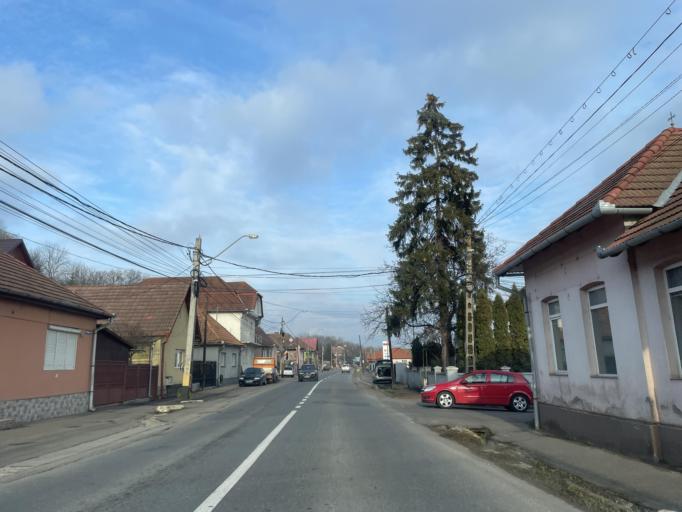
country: RO
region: Mures
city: Reghin-Sat
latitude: 46.7883
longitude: 24.7109
